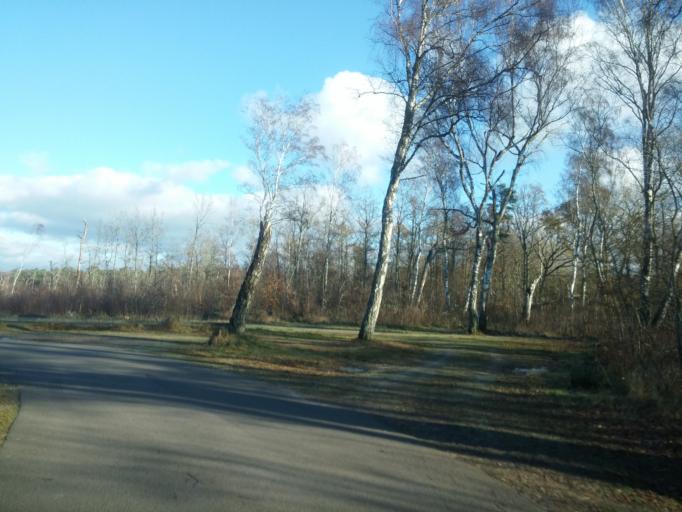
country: SE
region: Skane
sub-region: Angelholms Kommun
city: AEngelholm
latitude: 56.2358
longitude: 12.8184
